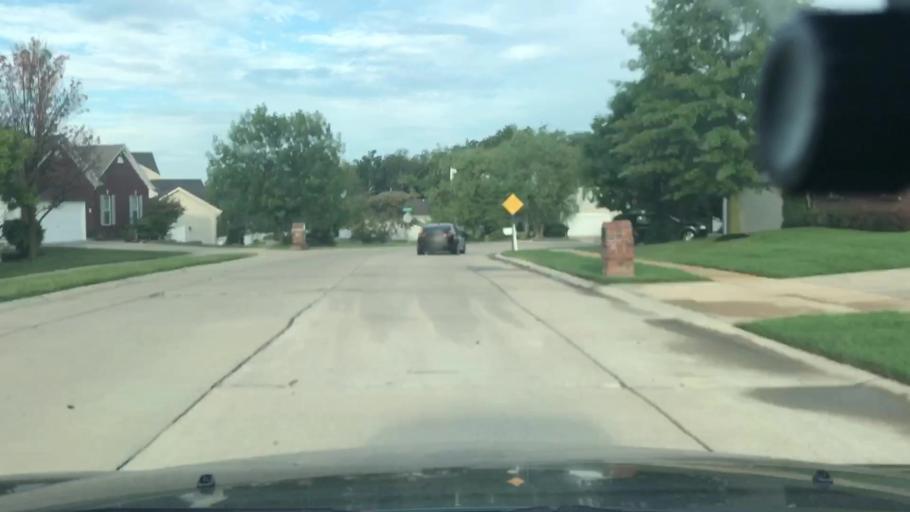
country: US
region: Missouri
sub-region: Saint Charles County
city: Wentzville
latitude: 38.8122
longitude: -90.8872
